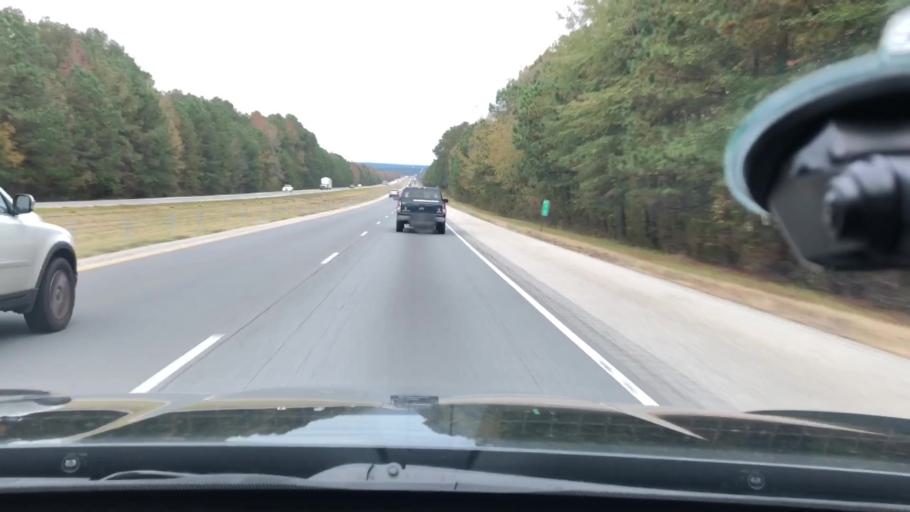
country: US
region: Arkansas
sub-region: Clark County
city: Arkadelphia
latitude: 34.1473
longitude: -93.0790
